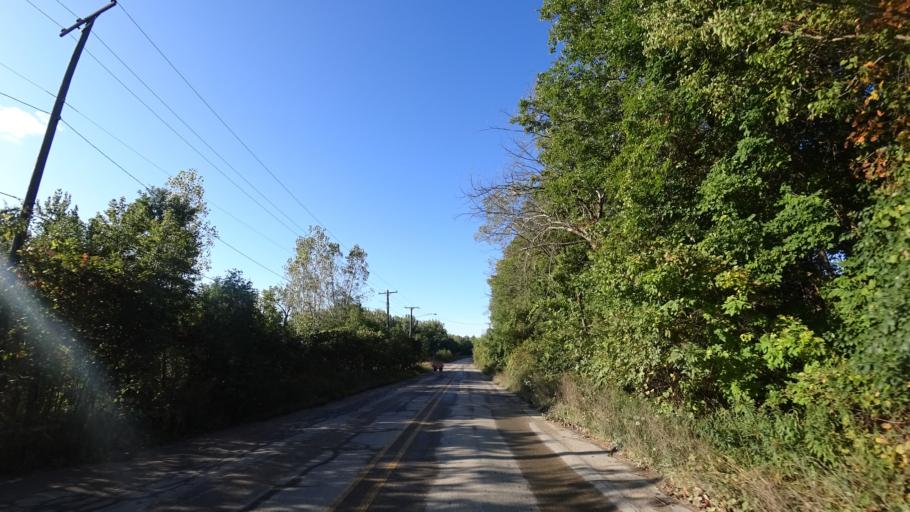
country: US
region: Michigan
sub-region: Kent County
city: Wyoming
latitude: 42.9510
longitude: -85.7107
